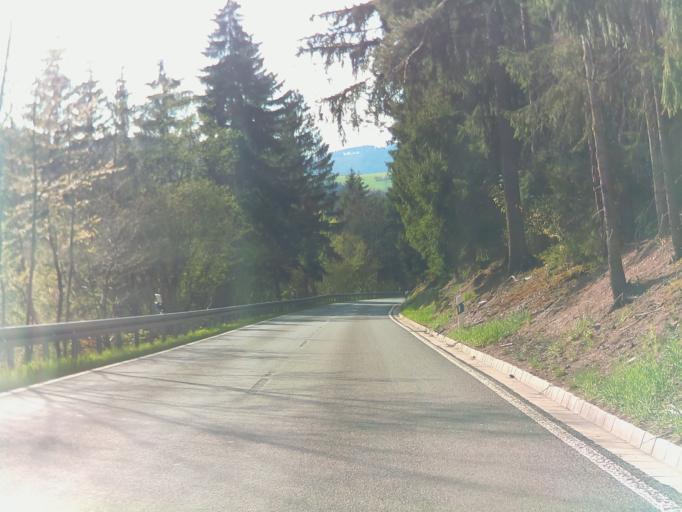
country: DE
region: Thuringia
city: Grafenthal
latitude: 50.5069
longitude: 11.3017
